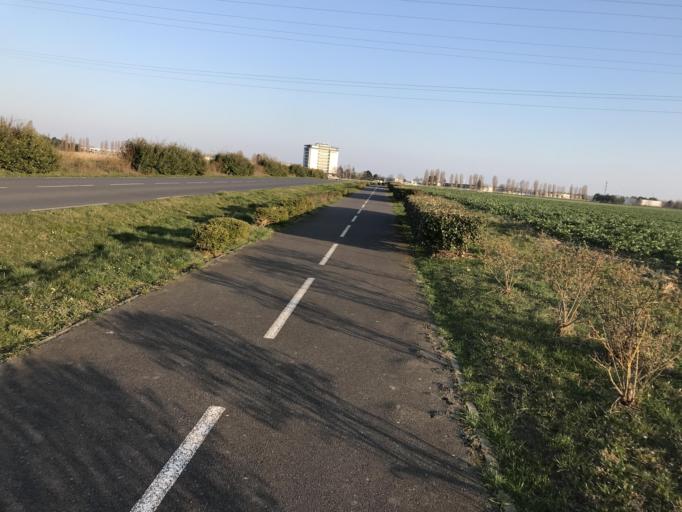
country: FR
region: Ile-de-France
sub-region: Departement de l'Essonne
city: Villejust
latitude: 48.6705
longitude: 2.2288
